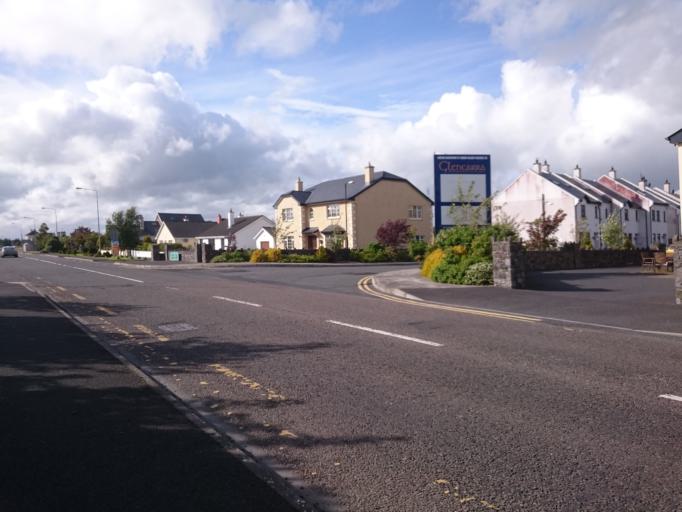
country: IE
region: Connaught
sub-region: Maigh Eo
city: Kiltamagh
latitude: 53.7962
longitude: -8.9207
